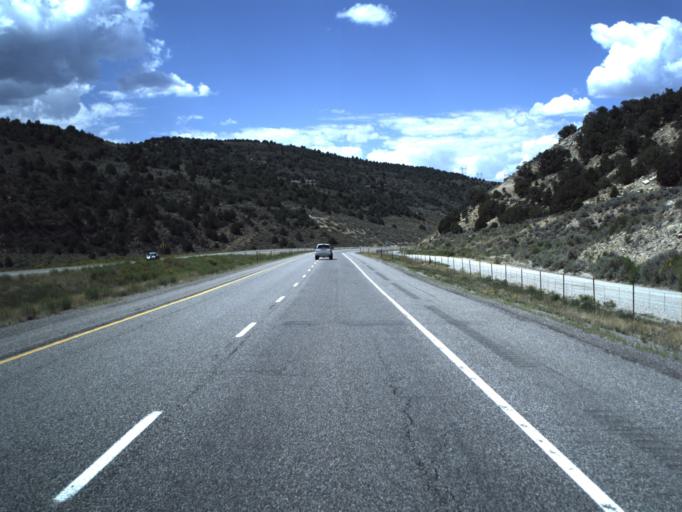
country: US
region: Utah
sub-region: Sevier County
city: Salina
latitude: 38.8038
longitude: -111.5246
